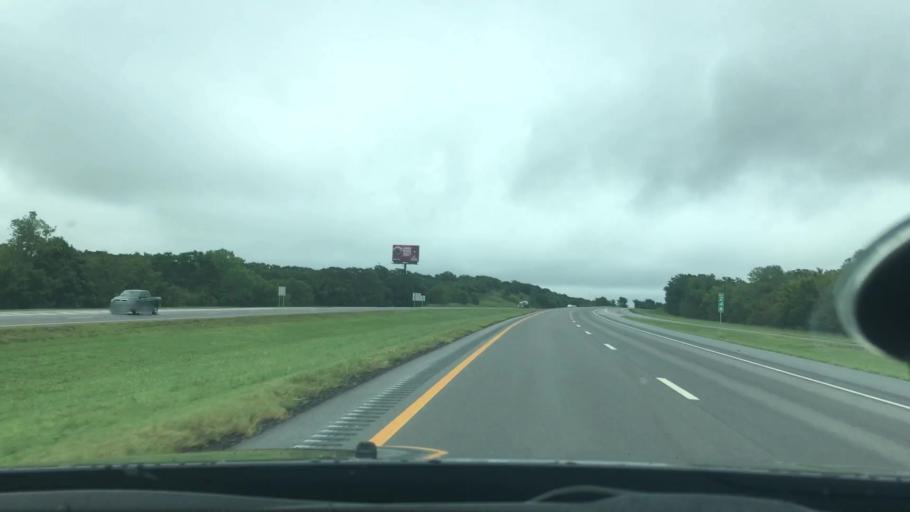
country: US
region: Oklahoma
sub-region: Okmulgee County
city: Henryetta
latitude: 35.4357
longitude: -95.8380
